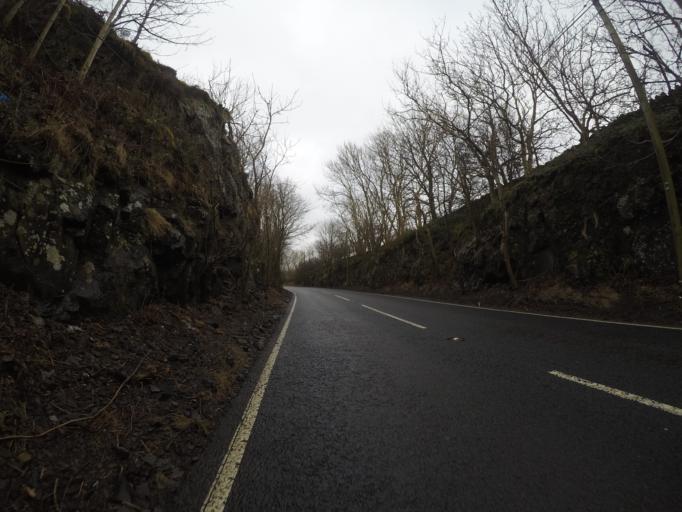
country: GB
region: Scotland
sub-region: North Ayrshire
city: Fairlie
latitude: 55.7772
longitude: -4.8413
